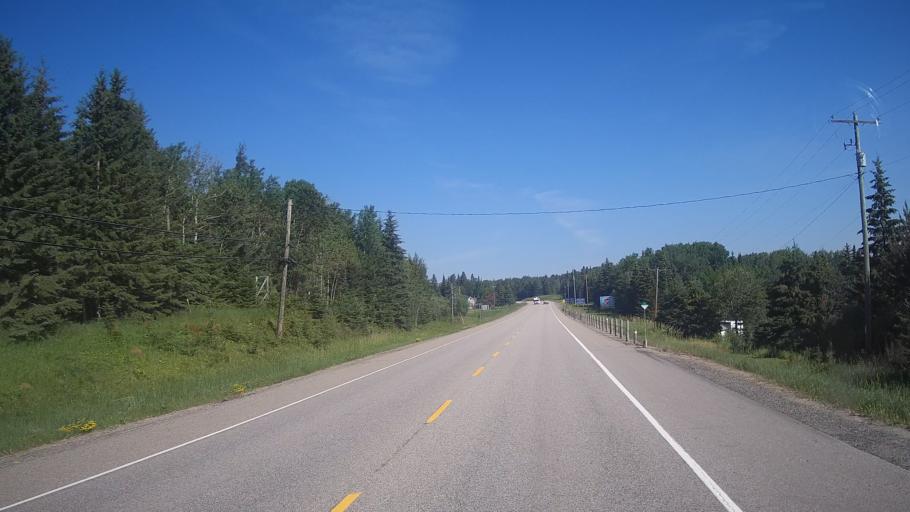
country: CA
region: Ontario
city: Dryden
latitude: 49.7789
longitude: -92.6967
